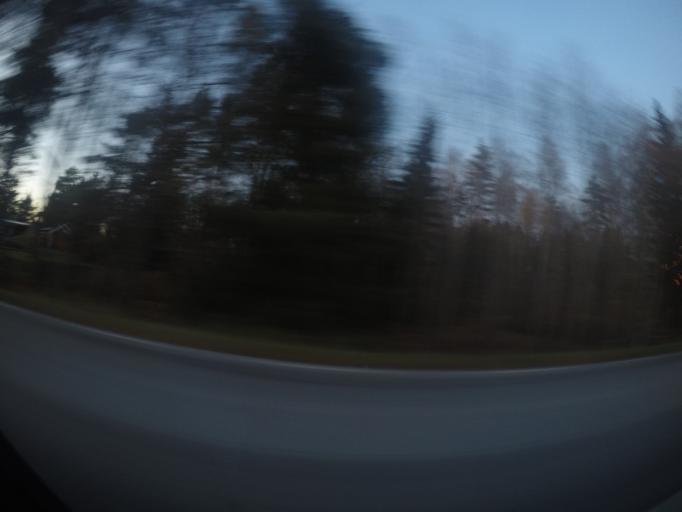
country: SE
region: OErebro
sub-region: Lindesbergs Kommun
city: Fellingsbro
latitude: 59.3261
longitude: 15.4597
